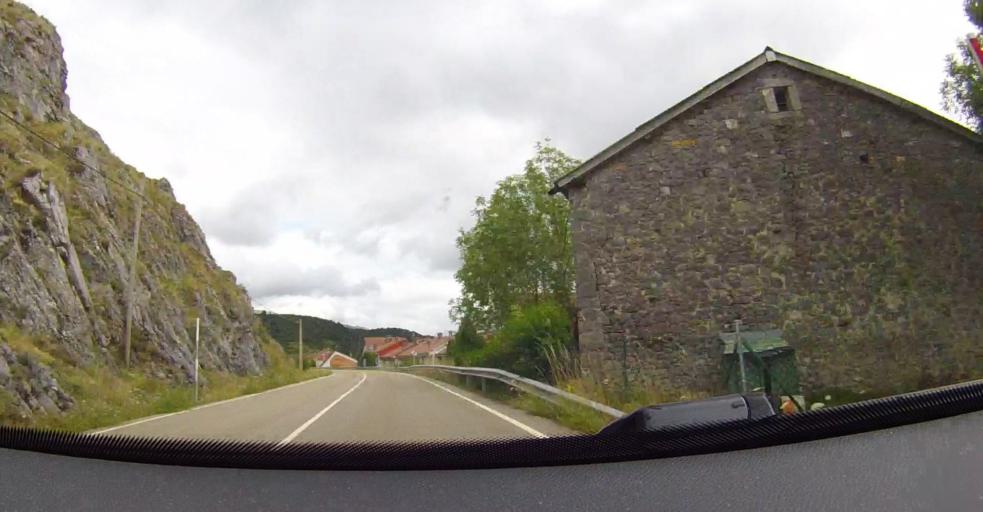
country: ES
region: Castille and Leon
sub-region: Provincia de Leon
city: Buron
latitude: 43.0255
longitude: -5.0552
